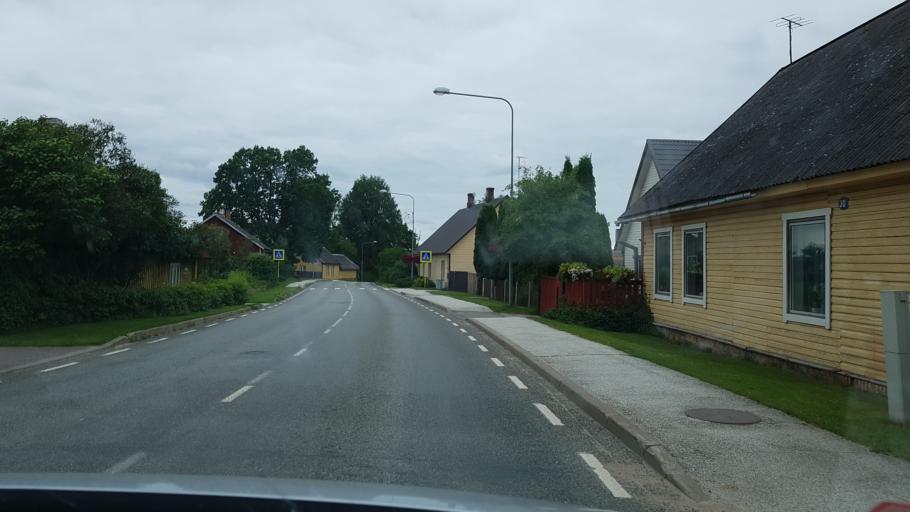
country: EE
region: Vorumaa
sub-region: Antsla vald
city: Vana-Antsla
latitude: 57.9875
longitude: 26.7535
